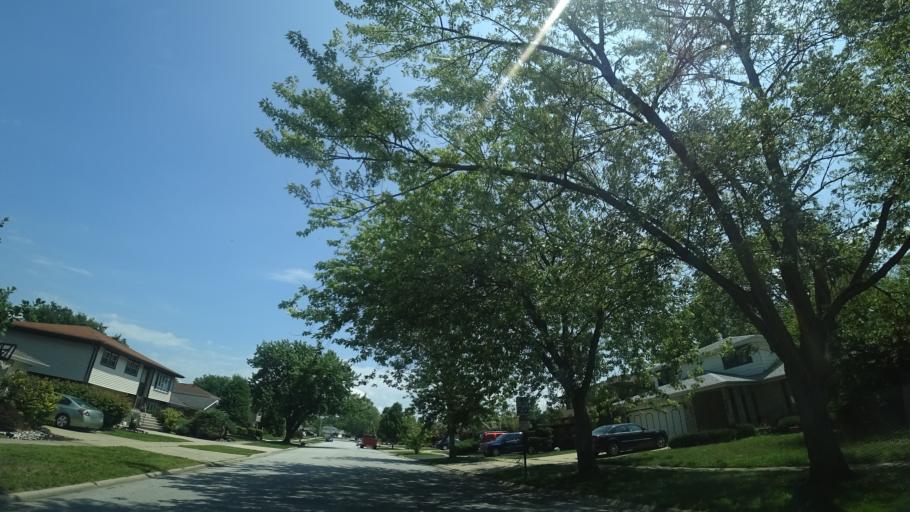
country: US
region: Illinois
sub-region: Cook County
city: Crestwood
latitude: 41.6667
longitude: -87.7679
